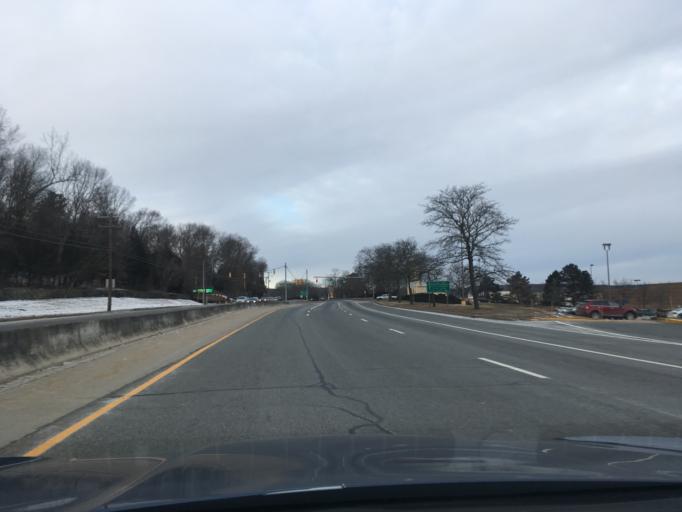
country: US
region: Rhode Island
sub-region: Kent County
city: West Warwick
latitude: 41.7167
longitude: -71.4772
